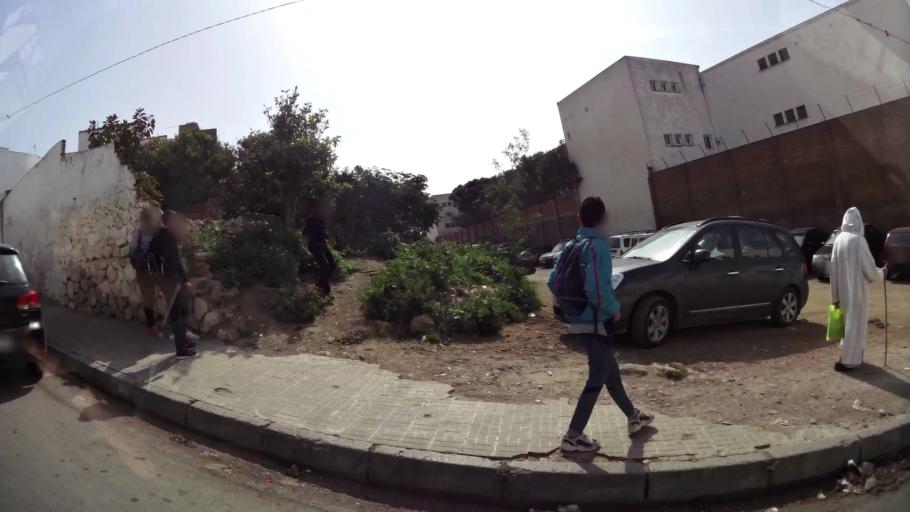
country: MA
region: Tanger-Tetouan
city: Tetouan
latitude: 35.5736
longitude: -5.3781
